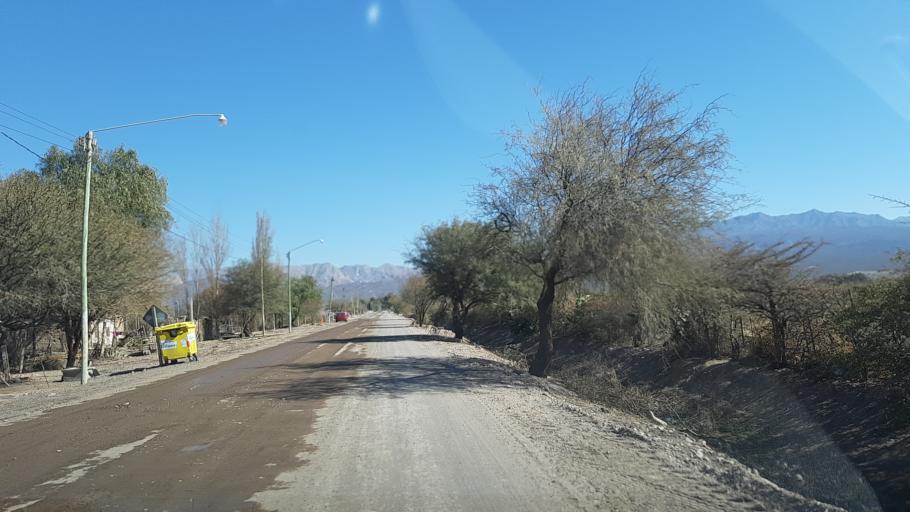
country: AR
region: San Juan
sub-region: Departamento de Zonda
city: Zonda
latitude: -31.4691
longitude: -68.7234
